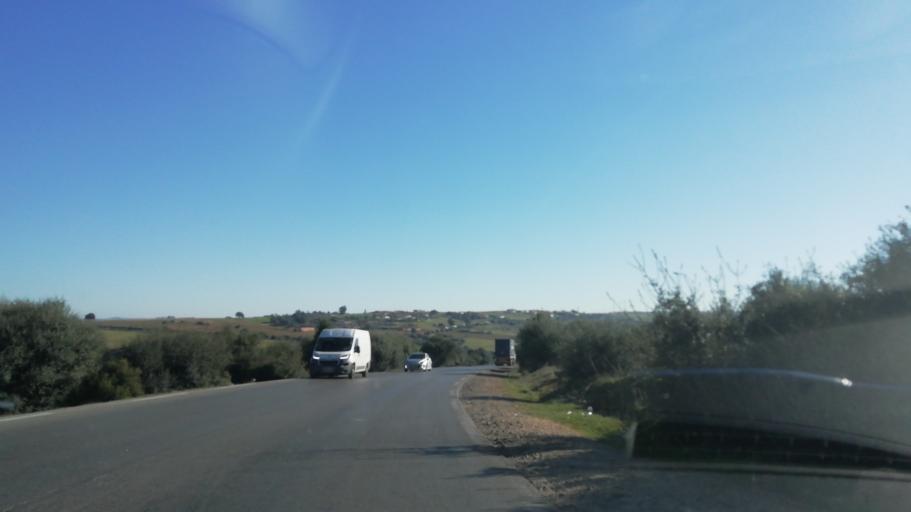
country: DZ
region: Relizane
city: Smala
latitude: 35.6895
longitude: 0.7944
